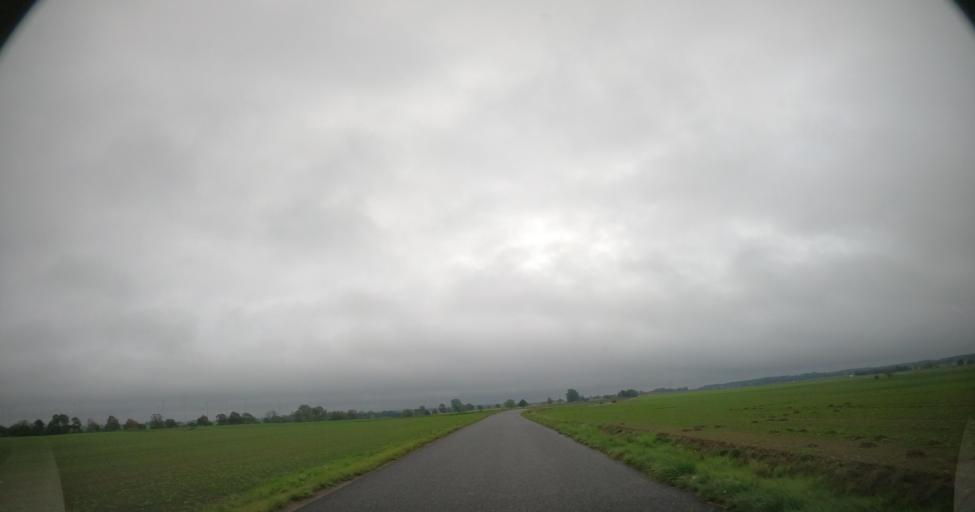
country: PL
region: West Pomeranian Voivodeship
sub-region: Powiat pyrzycki
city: Kozielice
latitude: 53.1150
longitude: 14.7622
